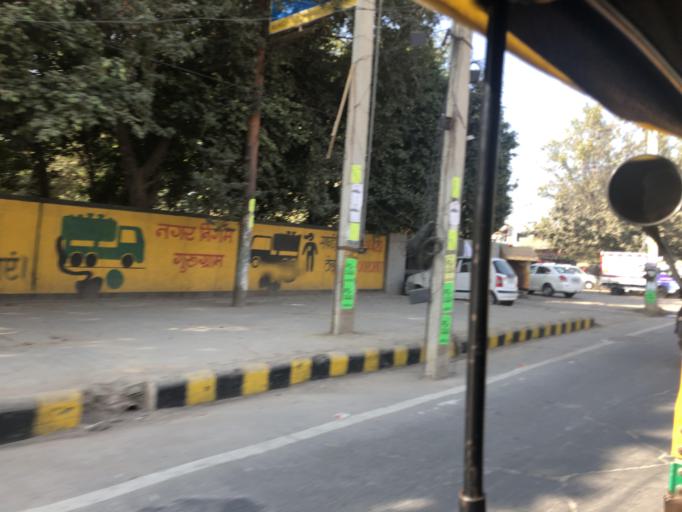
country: IN
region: Haryana
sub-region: Gurgaon
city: Gurgaon
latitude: 28.4474
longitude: 77.0747
